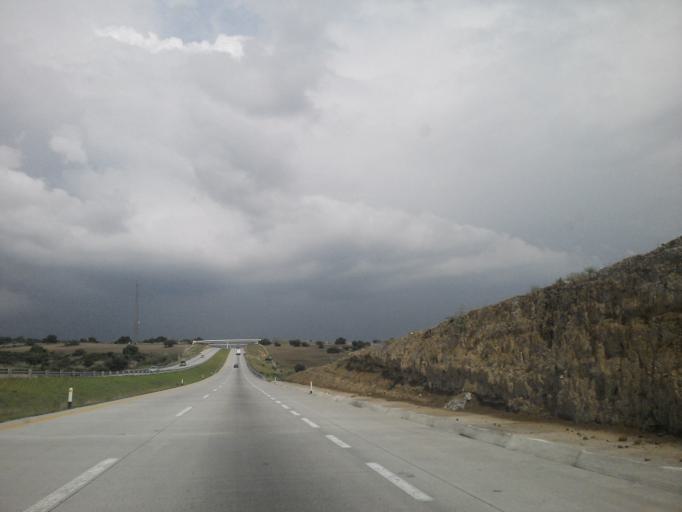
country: MX
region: Mexico
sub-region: Apaxco
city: Colonia Juarez
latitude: 19.9699
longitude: -99.1007
